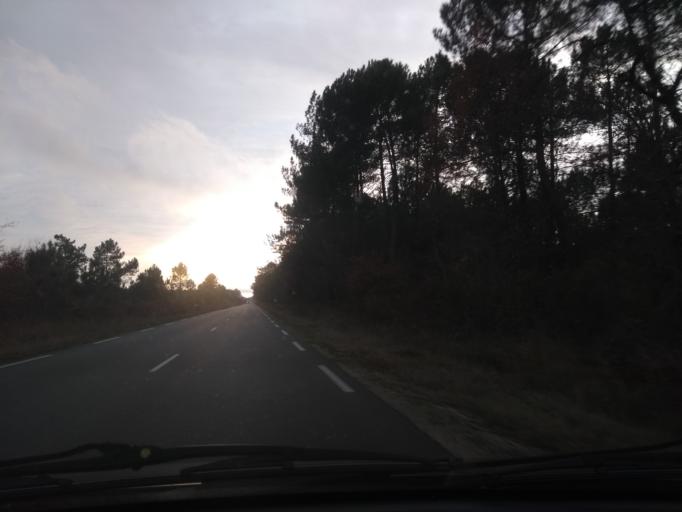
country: FR
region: Aquitaine
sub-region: Departement de la Gironde
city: Le Barp
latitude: 44.6045
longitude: -0.6989
